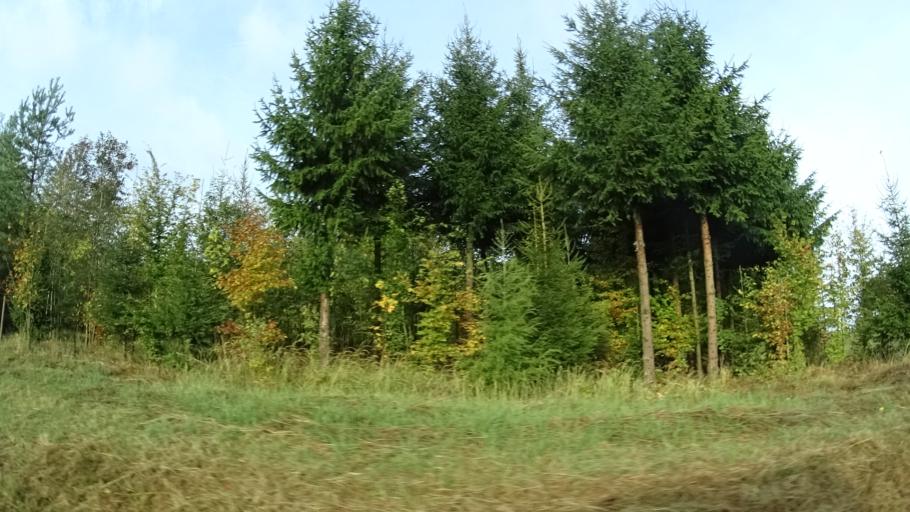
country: DE
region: Hesse
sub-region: Regierungsbezirk Giessen
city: Grebenhain
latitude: 50.4939
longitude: 9.3980
